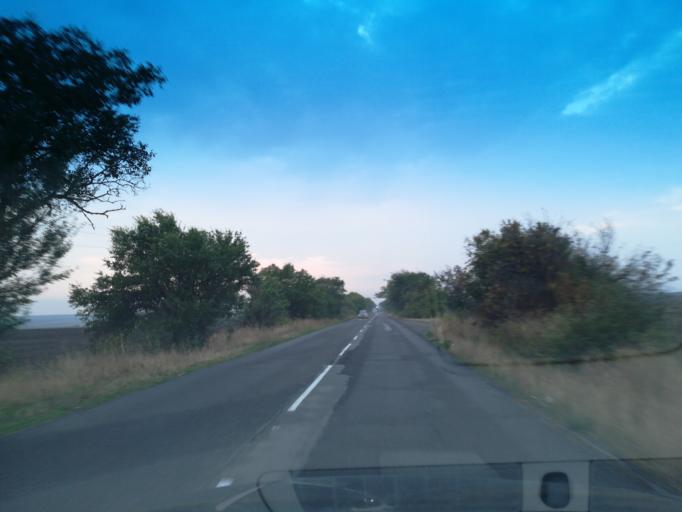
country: BG
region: Stara Zagora
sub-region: Obshtina Chirpan
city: Chirpan
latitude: 42.1921
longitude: 25.2940
